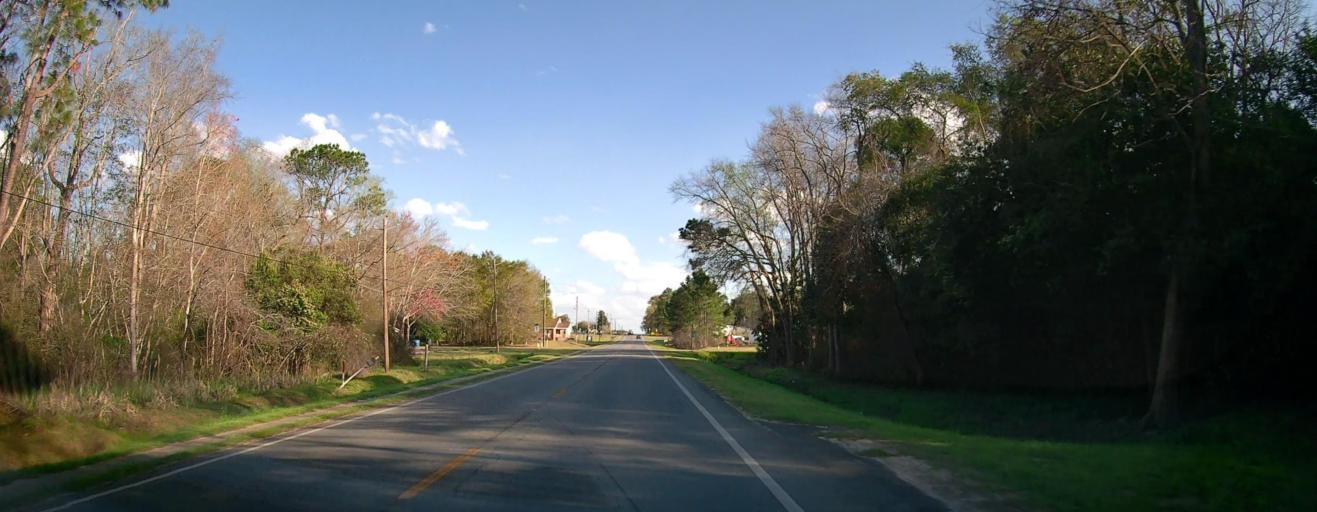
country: US
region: Georgia
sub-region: Toombs County
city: Lyons
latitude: 32.1981
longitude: -82.3134
